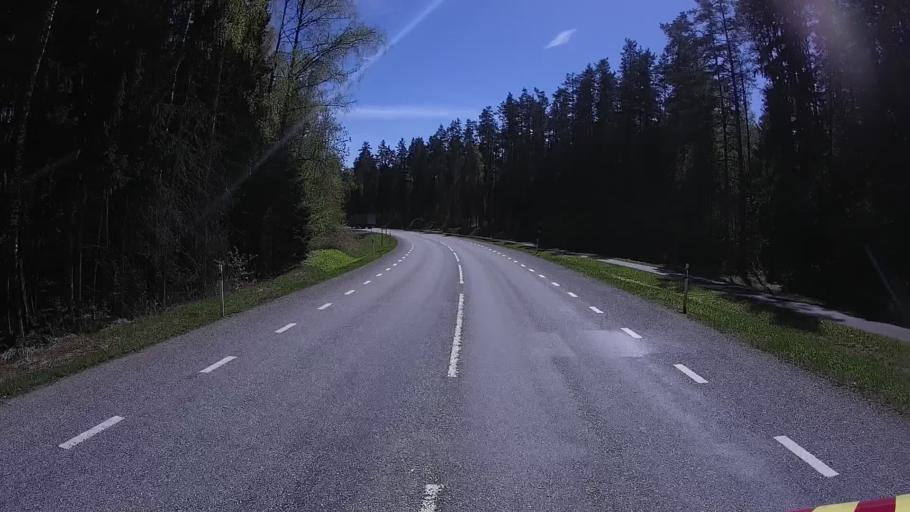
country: EE
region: Harju
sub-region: Kuusalu vald
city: Kuusalu
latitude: 59.2647
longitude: 25.6558
